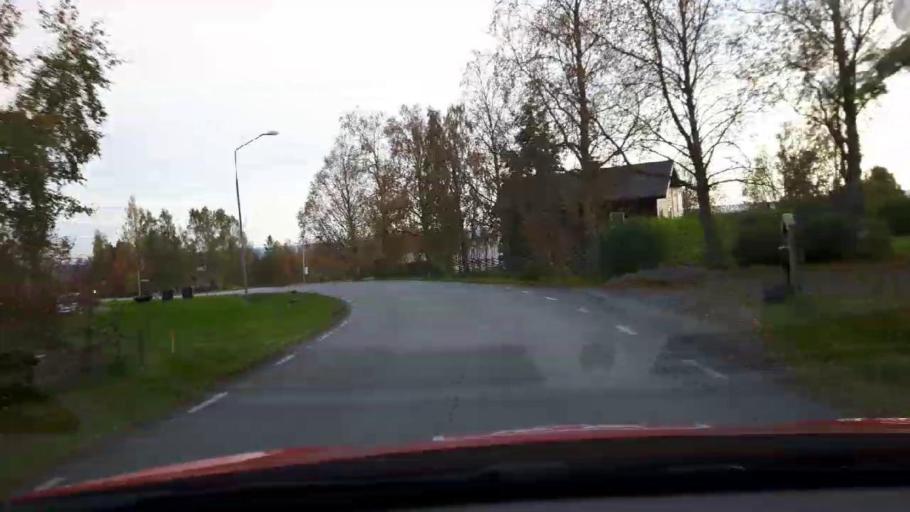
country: SE
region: Jaemtland
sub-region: Krokoms Kommun
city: Krokom
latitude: 63.3668
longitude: 14.4783
